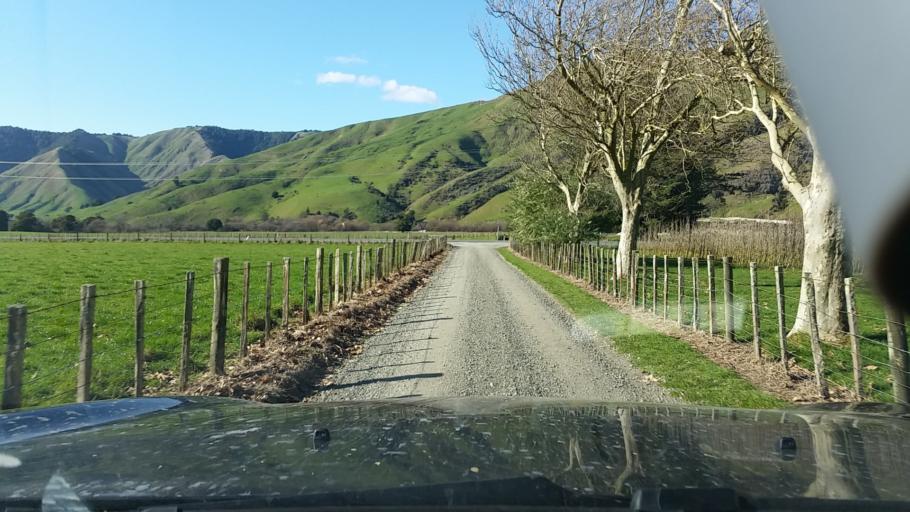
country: NZ
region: Marlborough
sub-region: Marlborough District
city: Picton
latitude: -41.3186
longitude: 173.7639
